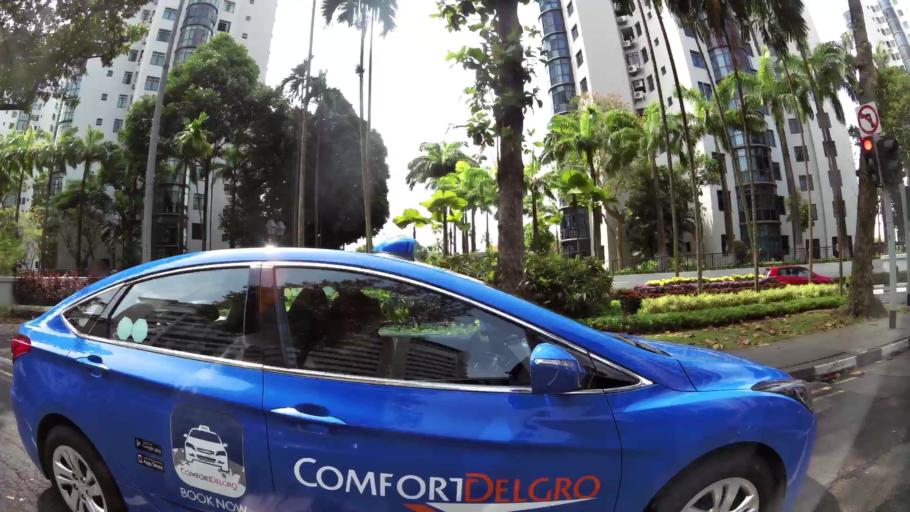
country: MY
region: Johor
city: Johor Bahru
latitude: 1.3445
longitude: 103.7338
